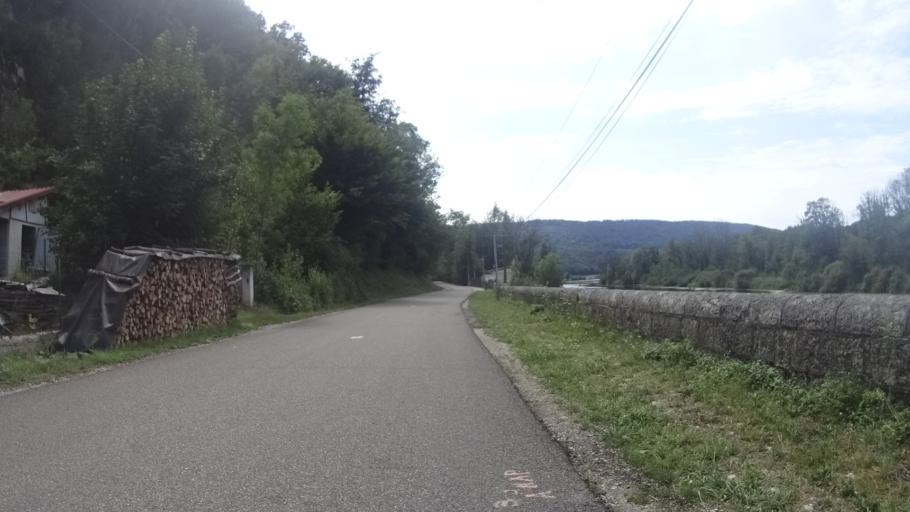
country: FR
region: Franche-Comte
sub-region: Departement du Doubs
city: Clerval
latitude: 47.3810
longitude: 6.5051
